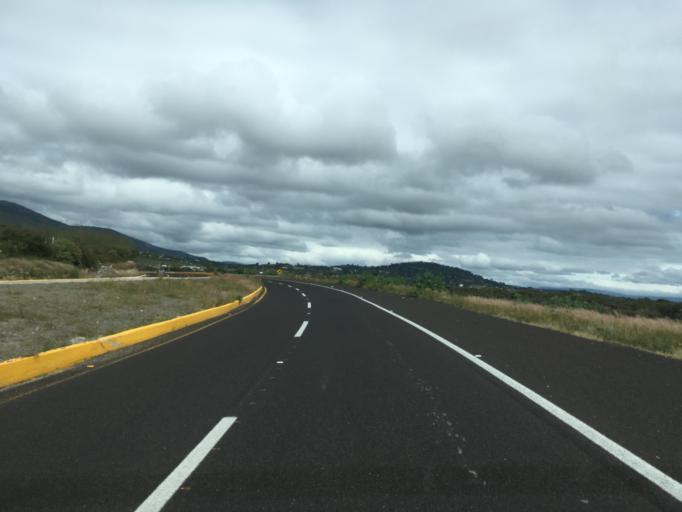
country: MX
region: Hidalgo
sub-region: Atotonilco el Grande
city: Santa Maria Amajac
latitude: 20.3760
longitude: -98.7197
